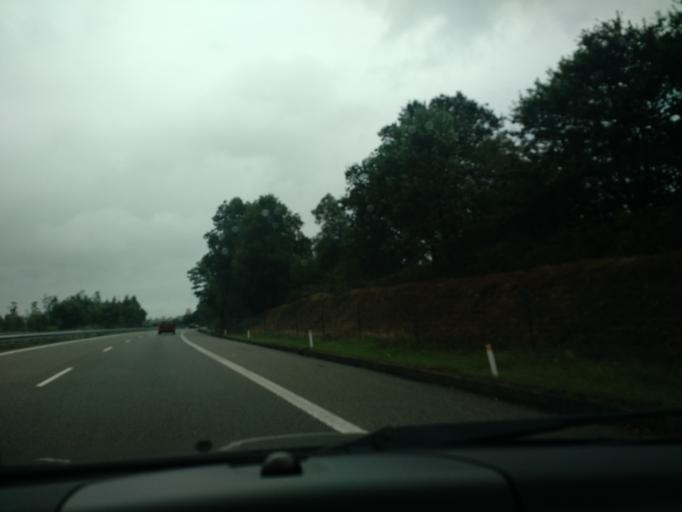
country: ES
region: Galicia
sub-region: Provincia da Coruna
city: Mesia
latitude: 43.1166
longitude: -8.3328
